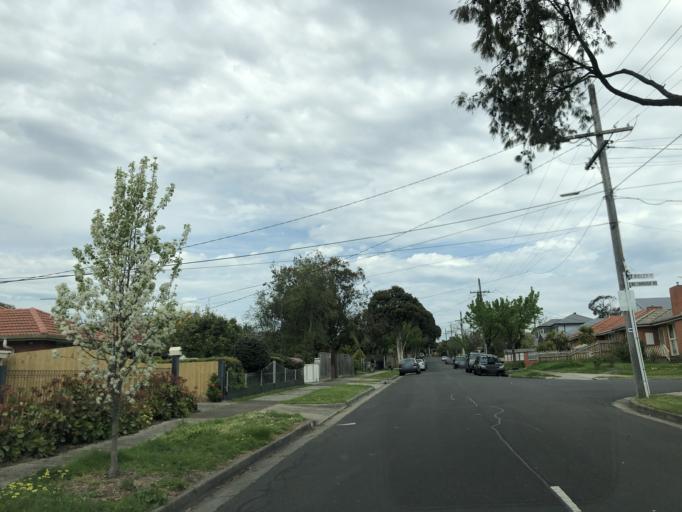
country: AU
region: Victoria
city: Burwood East
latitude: -37.8483
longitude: 145.1397
